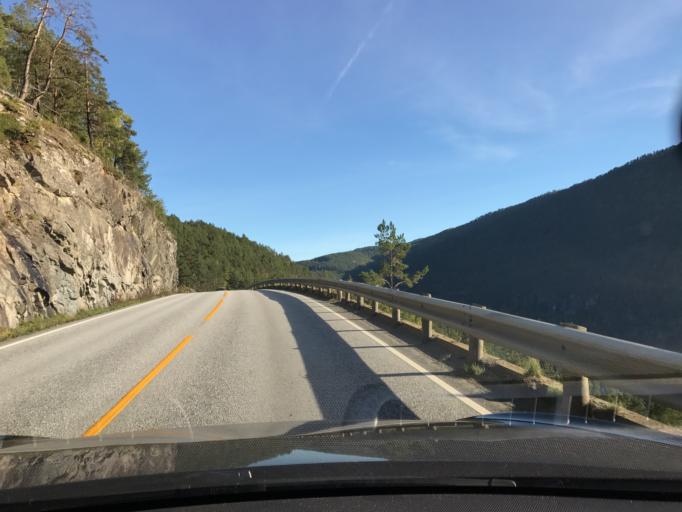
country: NO
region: Sogn og Fjordane
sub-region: Sogndal
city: Sogndalsfjora
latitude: 61.2102
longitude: 7.1520
